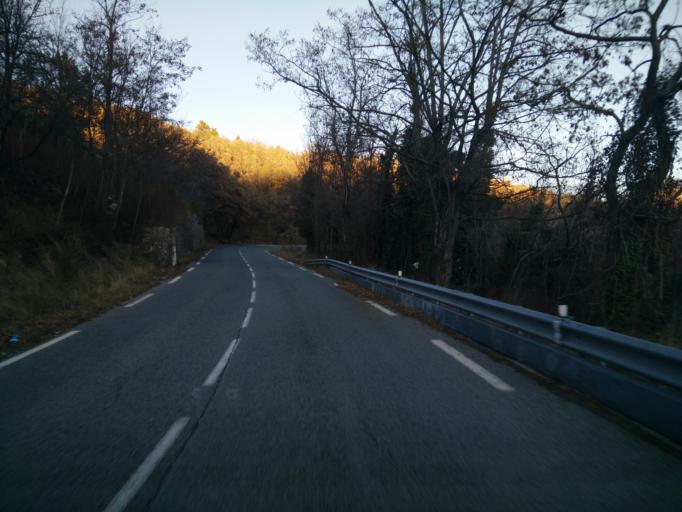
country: FR
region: Provence-Alpes-Cote d'Azur
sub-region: Departement du Var
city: Montferrat
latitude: 43.6276
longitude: 6.4836
